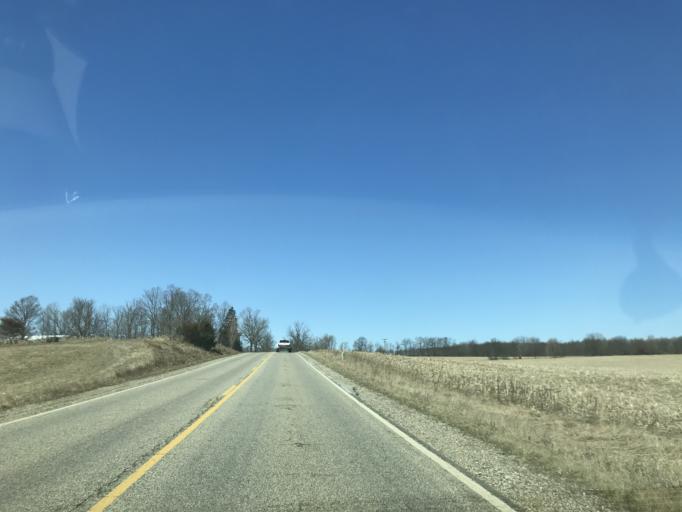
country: US
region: Michigan
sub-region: Hillsdale County
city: Litchfield
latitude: 41.9857
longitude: -84.7761
